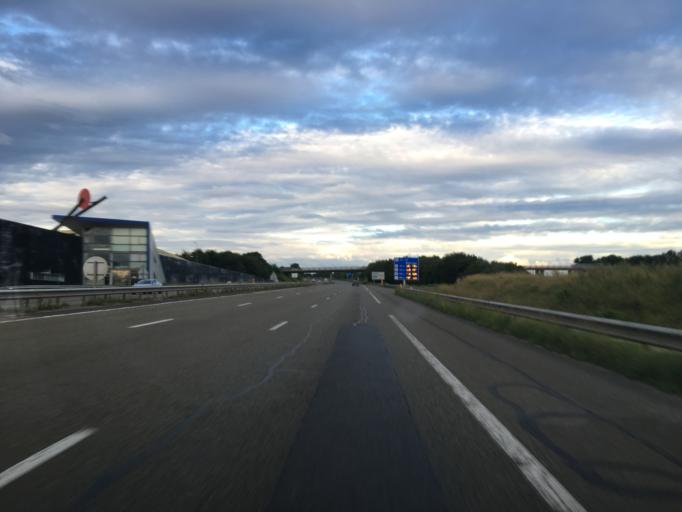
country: FR
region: Ile-de-France
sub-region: Departement de Seine-et-Marne
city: Voisenon
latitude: 48.5878
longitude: 2.6638
